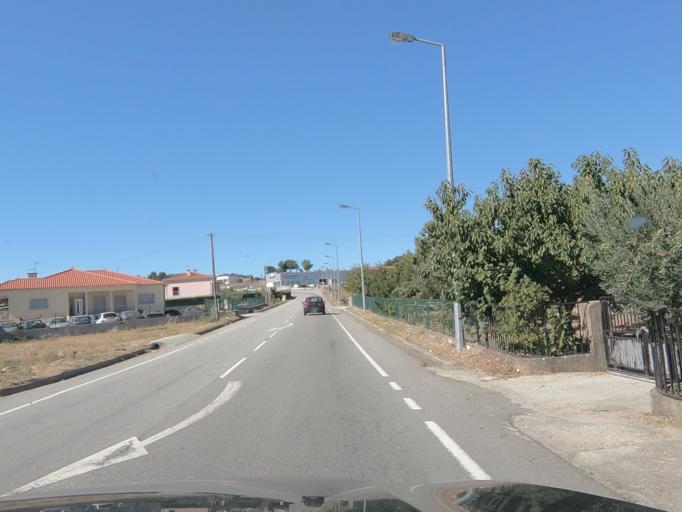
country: PT
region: Vila Real
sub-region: Valpacos
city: Valpacos
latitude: 41.6694
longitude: -7.3374
